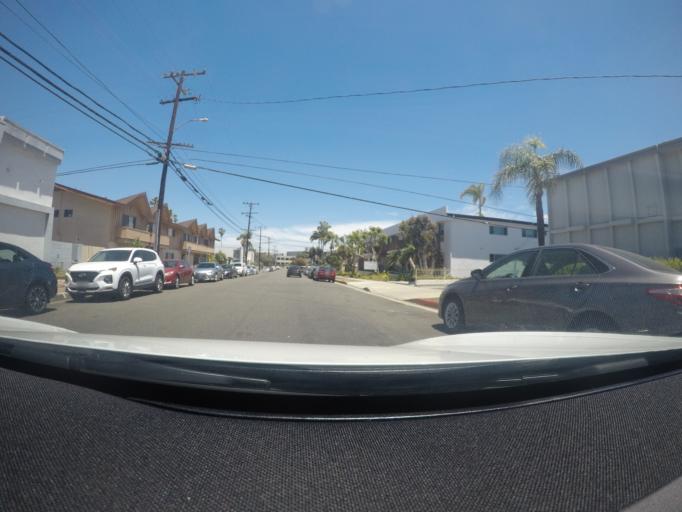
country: US
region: California
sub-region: Los Angeles County
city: Torrance
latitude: 33.8414
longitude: -118.3474
